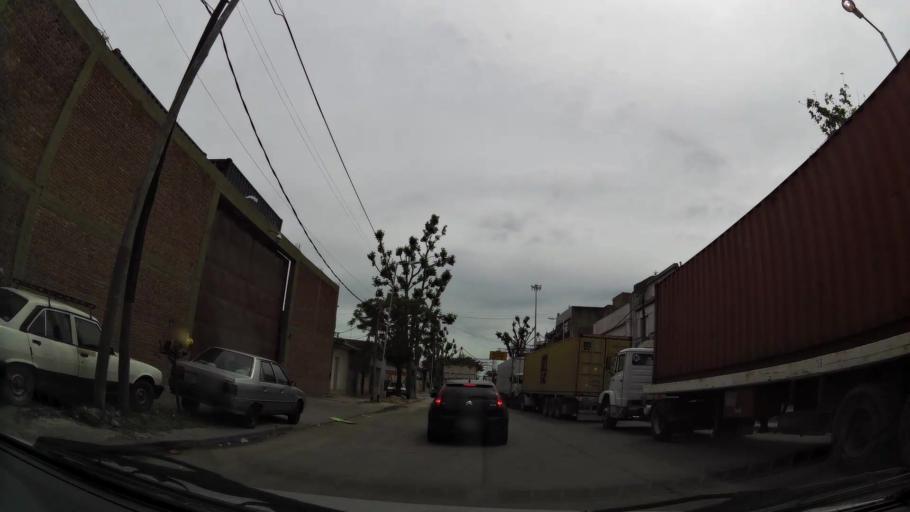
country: AR
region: Buenos Aires
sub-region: Partido de Avellaneda
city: Avellaneda
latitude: -34.6488
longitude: -58.3435
